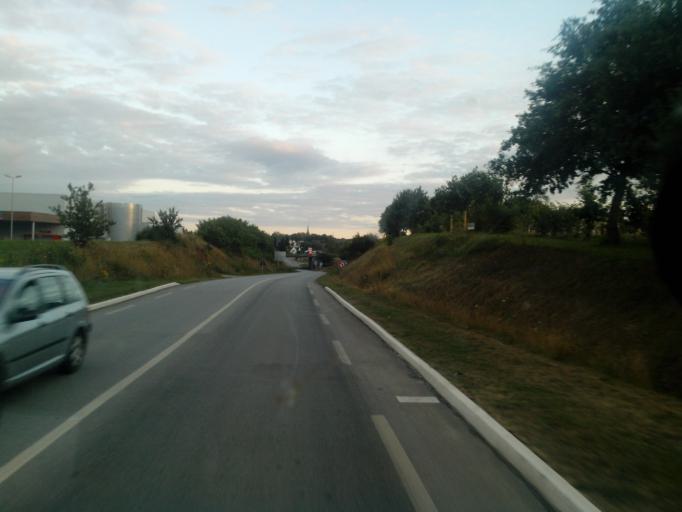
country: FR
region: Brittany
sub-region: Departement du Morbihan
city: Josselin
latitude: 47.9658
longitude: -2.5451
